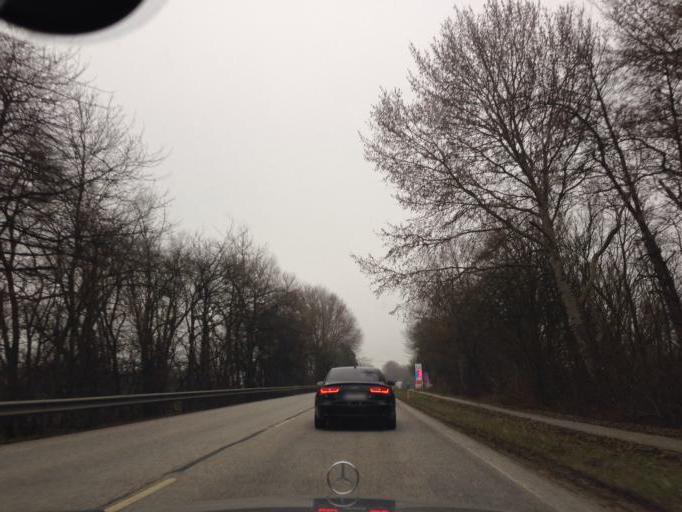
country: DE
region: Schleswig-Holstein
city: Kirchbarkau
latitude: 54.2143
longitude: 10.1483
